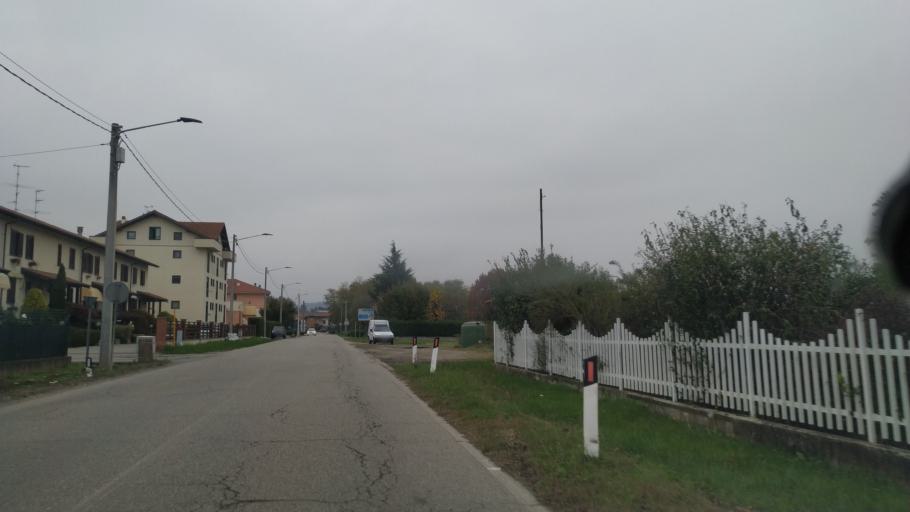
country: IT
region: Piedmont
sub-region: Provincia di Biella
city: Cerreto Castello
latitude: 45.5565
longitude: 8.1712
